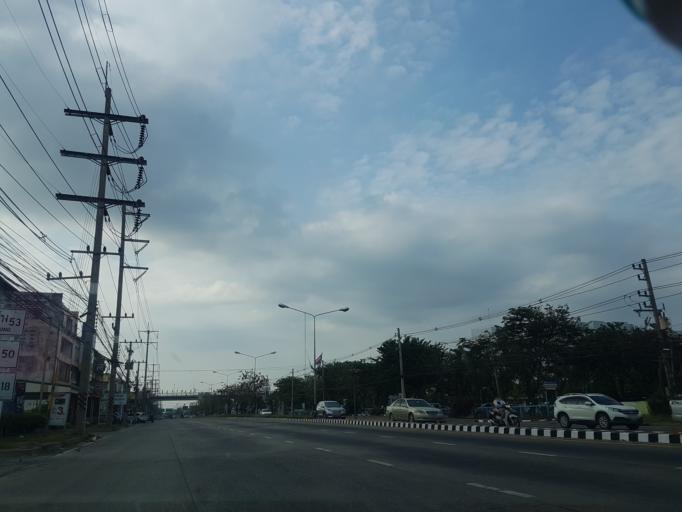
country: TH
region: Sara Buri
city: Phra Phutthabat
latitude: 14.7226
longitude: 100.8029
